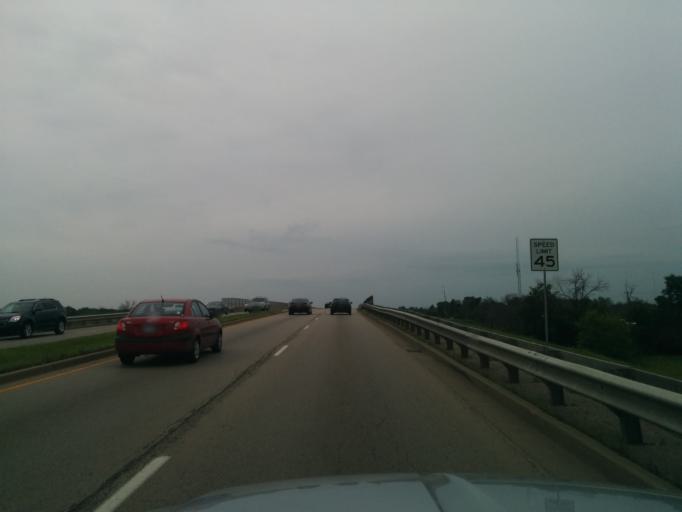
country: US
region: Illinois
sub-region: DuPage County
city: Warrenville
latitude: 41.7766
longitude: -88.2412
